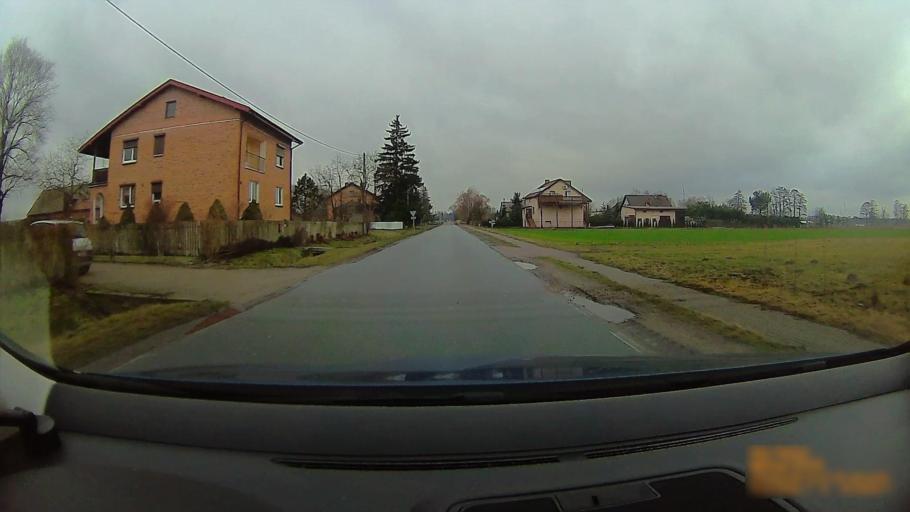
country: PL
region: Greater Poland Voivodeship
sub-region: Powiat koninski
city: Rychwal
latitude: 52.0955
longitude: 18.1642
